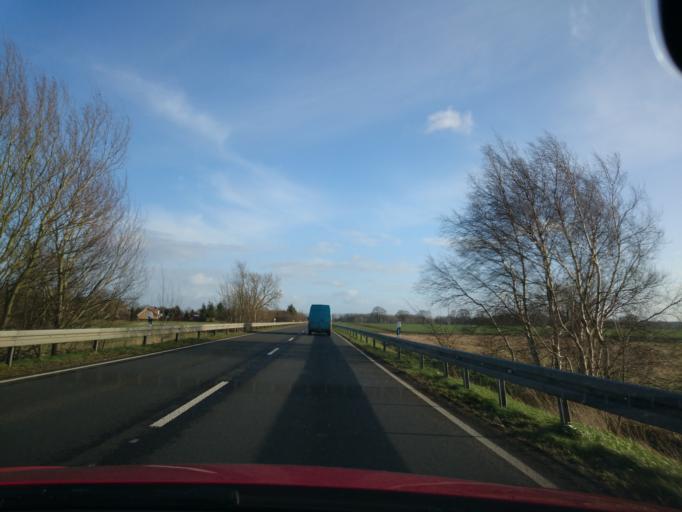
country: DE
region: Mecklenburg-Vorpommern
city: Mesekenhagen
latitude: 54.1564
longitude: 13.3098
